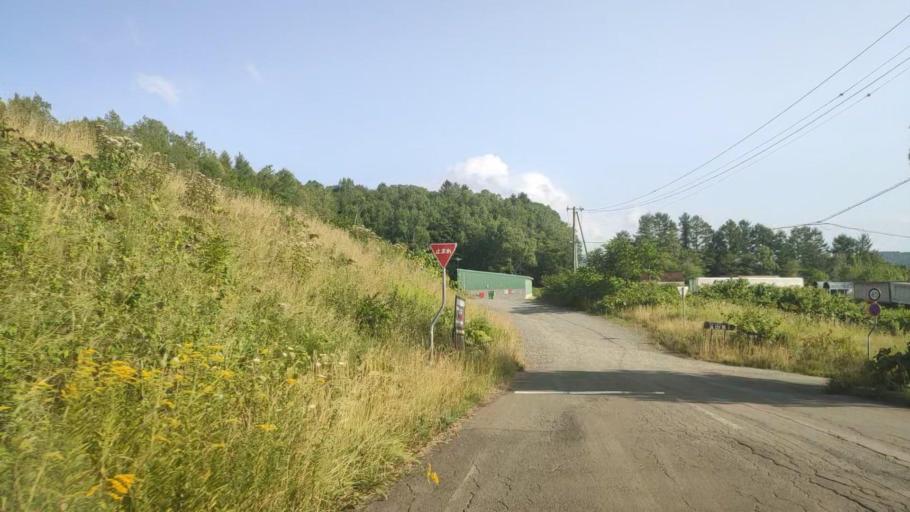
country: JP
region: Hokkaido
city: Shimo-furano
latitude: 43.3445
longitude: 142.3605
